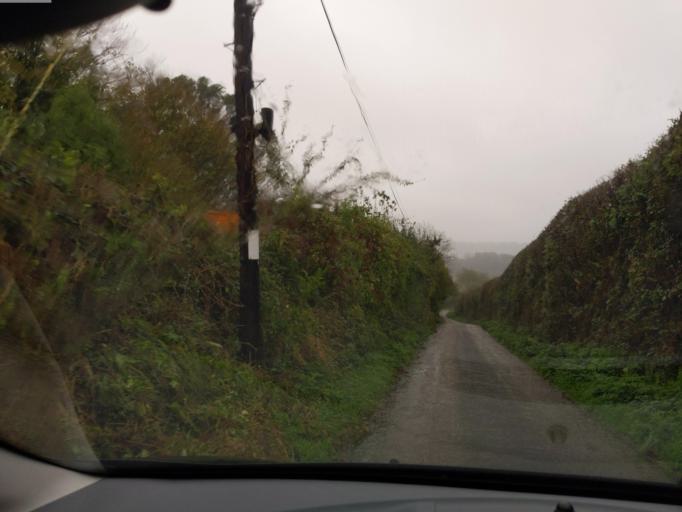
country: GB
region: England
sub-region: Devon
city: Bere Alston
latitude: 50.4698
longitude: -4.2384
